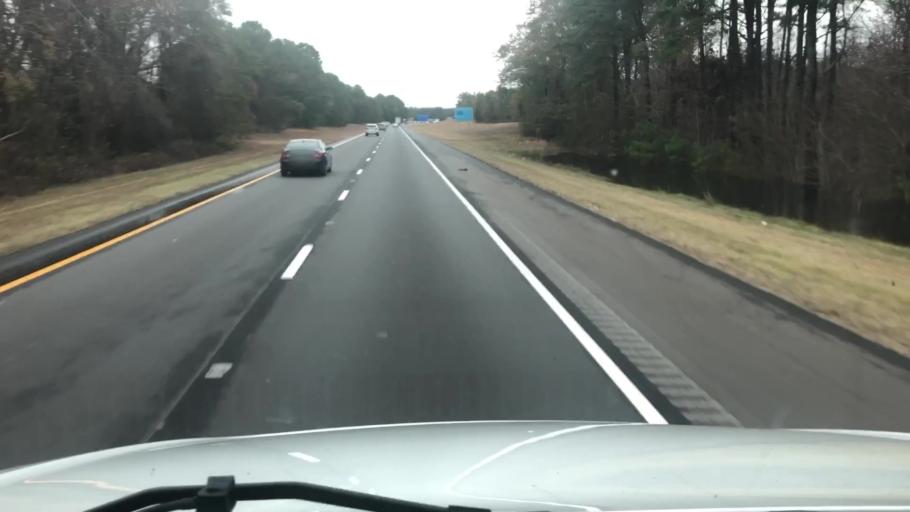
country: US
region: North Carolina
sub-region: Cumberland County
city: Eastover
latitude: 35.0703
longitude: -78.7916
